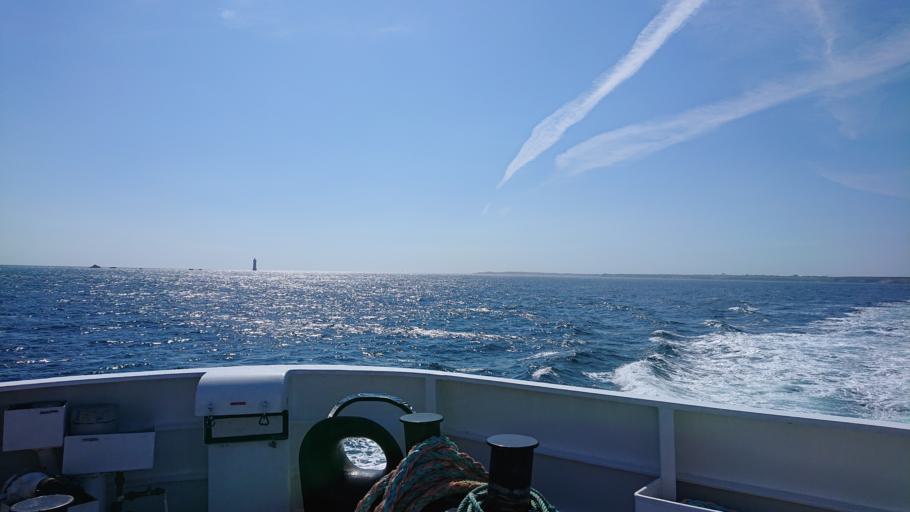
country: FR
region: Brittany
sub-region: Departement du Finistere
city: Porspoder
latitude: 48.4468
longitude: -4.9995
